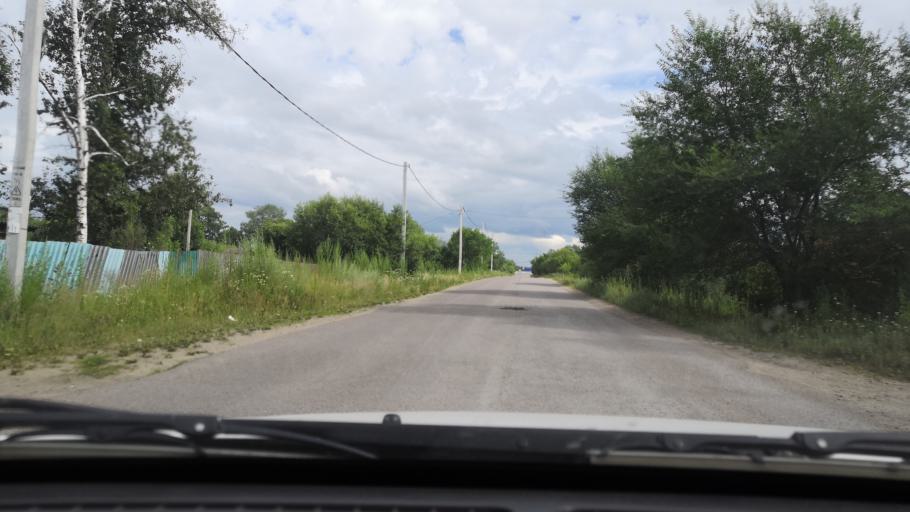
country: RU
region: Jewish Autonomous Oblast
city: Priamurskiy
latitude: 48.5219
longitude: 134.9067
